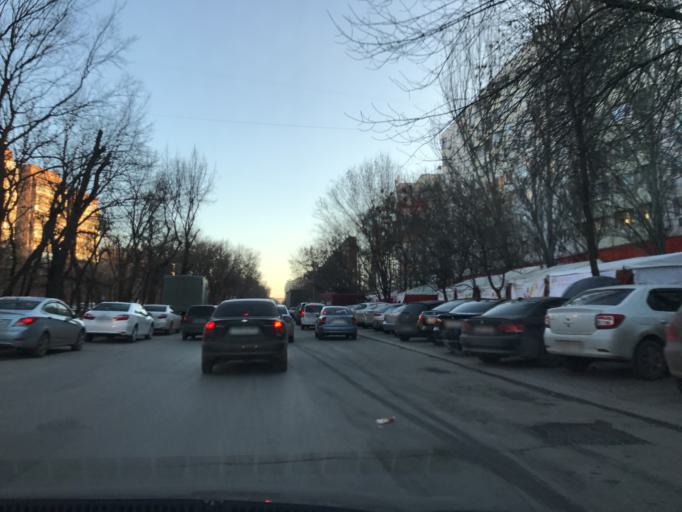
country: RU
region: Rostov
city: Rostov-na-Donu
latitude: 47.2308
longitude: 39.6292
